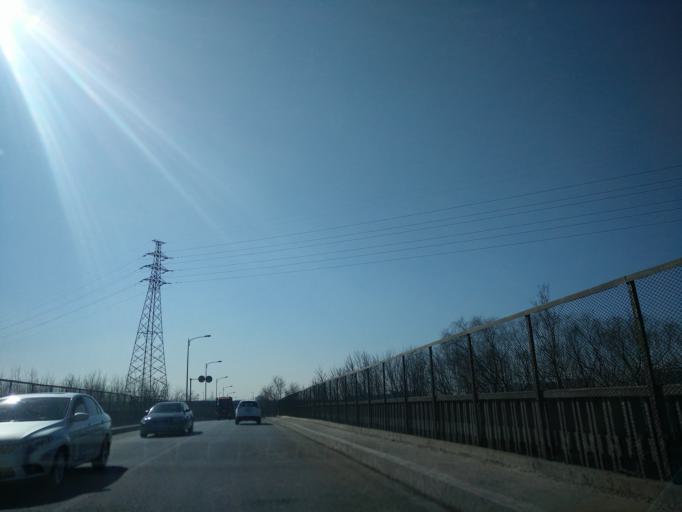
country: CN
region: Beijing
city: Jiugong
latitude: 39.7783
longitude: 116.5424
